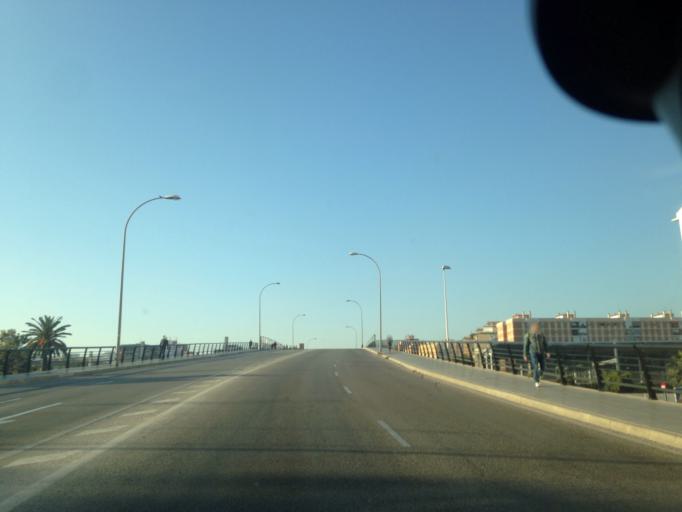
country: ES
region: Andalusia
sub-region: Provincia de Malaga
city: Malaga
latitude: 36.7084
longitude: -4.4358
